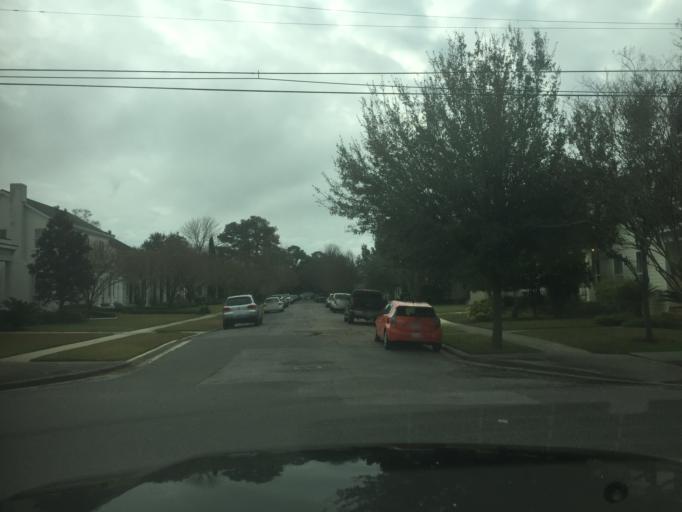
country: US
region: Louisiana
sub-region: Jefferson Parish
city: Metairie
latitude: 29.9992
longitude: -90.1074
